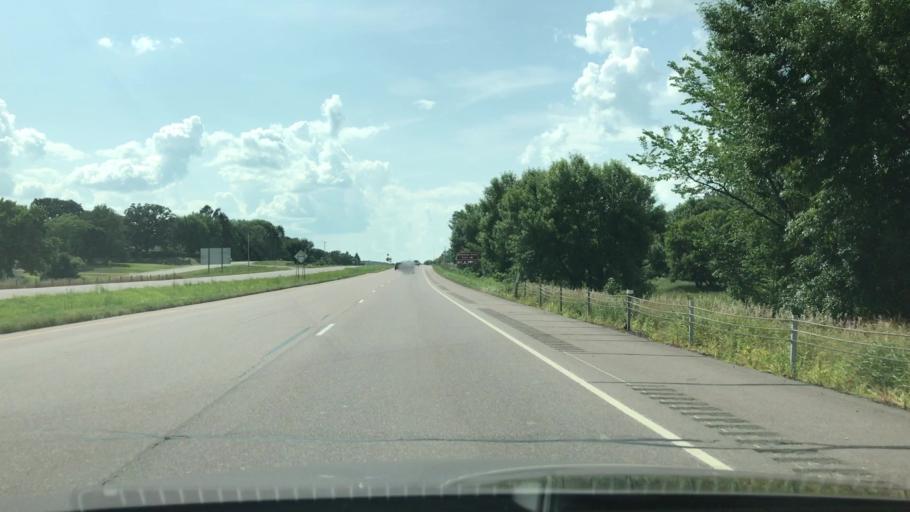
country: US
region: Minnesota
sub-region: Nicollet County
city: North Mankato
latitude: 44.1524
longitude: -94.0561
